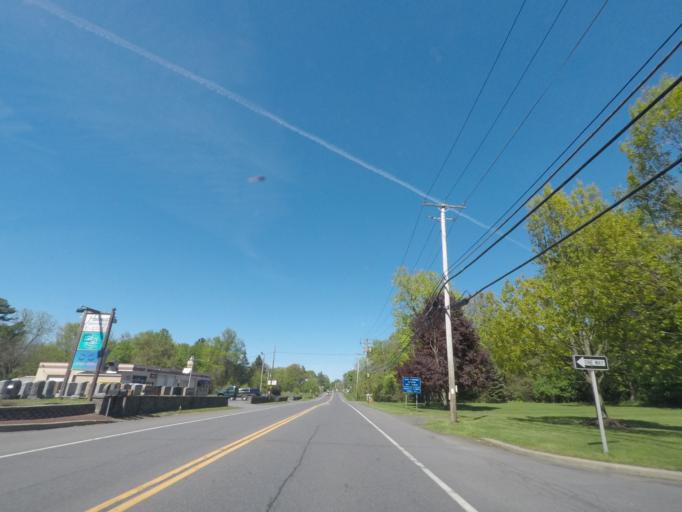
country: US
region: New York
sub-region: Ulster County
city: Saugerties South
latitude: 42.0607
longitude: -73.9520
